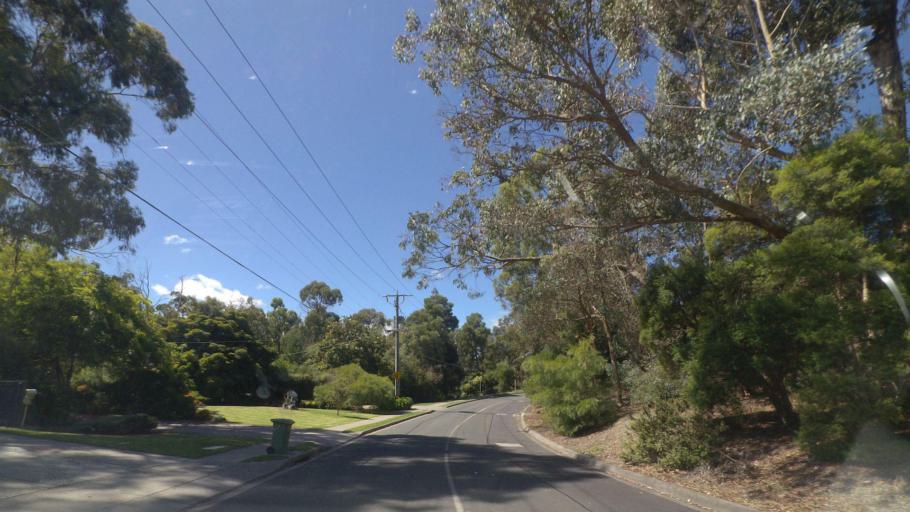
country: AU
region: Victoria
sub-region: Maroondah
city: Croydon Hills
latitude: -37.7691
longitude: 145.2766
